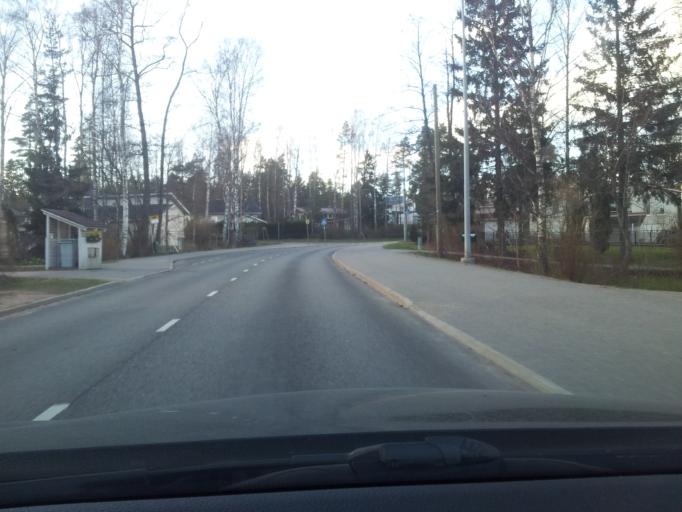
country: FI
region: Uusimaa
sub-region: Helsinki
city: Espoo
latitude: 60.1423
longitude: 24.6830
